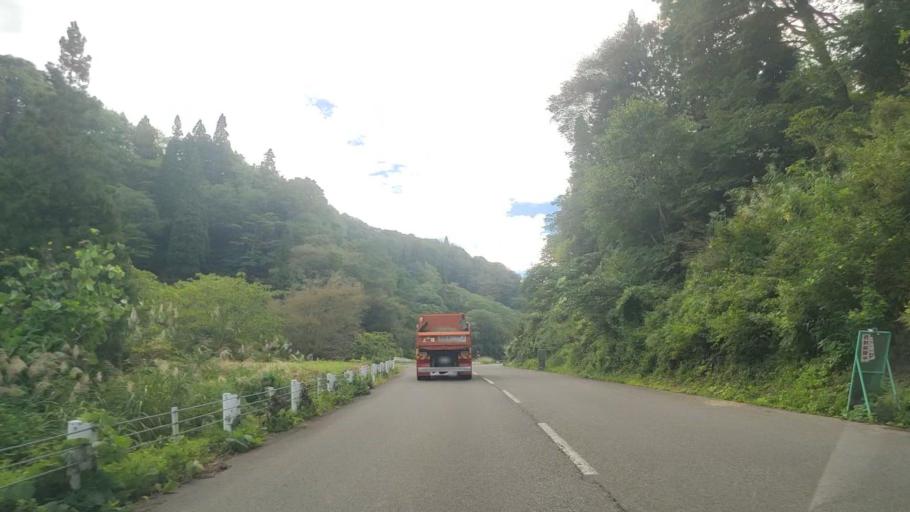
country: JP
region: Nagano
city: Iiyama
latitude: 36.8977
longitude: 138.3198
